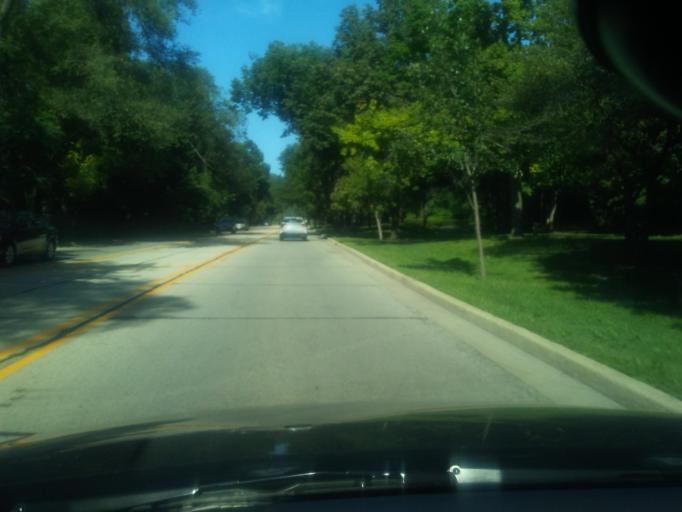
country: US
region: Illinois
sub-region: Cook County
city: Evanston
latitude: 42.0540
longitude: -87.7072
